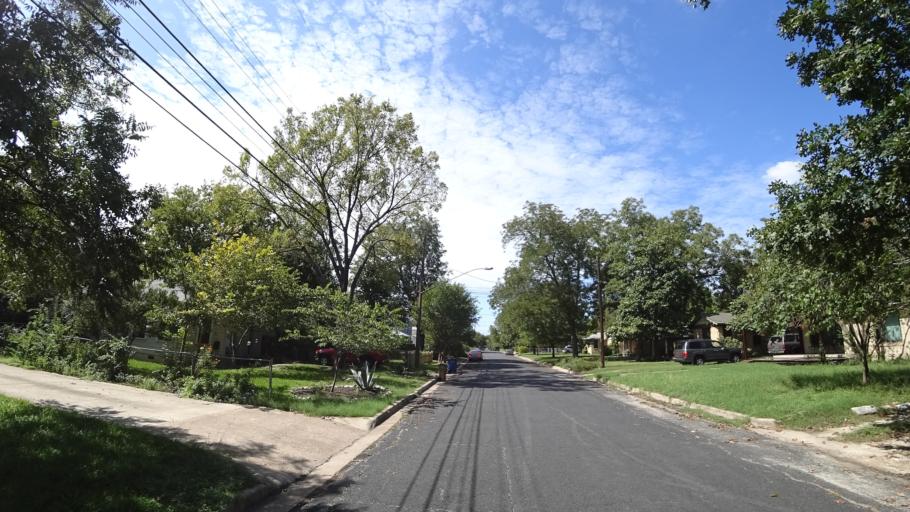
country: US
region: Texas
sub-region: Travis County
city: Austin
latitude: 30.3405
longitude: -97.7241
